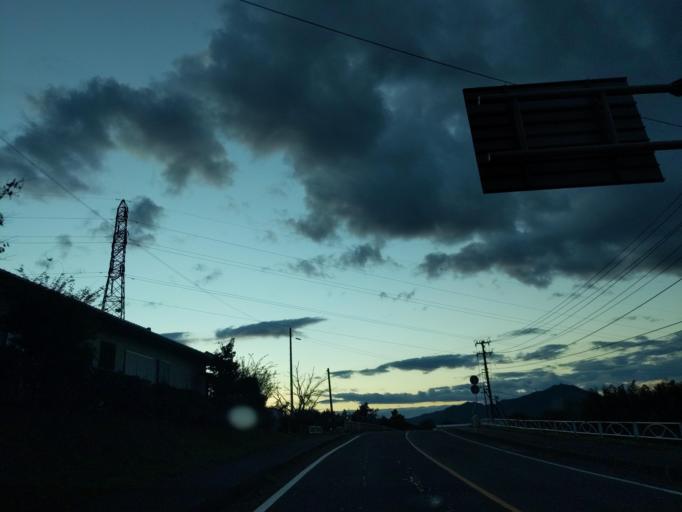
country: JP
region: Fukushima
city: Motomiya
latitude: 37.5021
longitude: 140.4004
